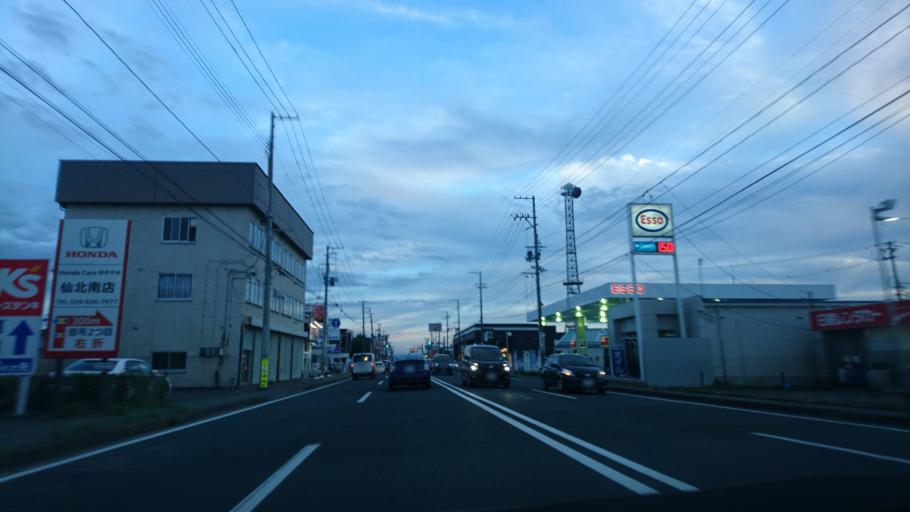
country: JP
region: Iwate
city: Morioka-shi
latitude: 39.6700
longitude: 141.1566
